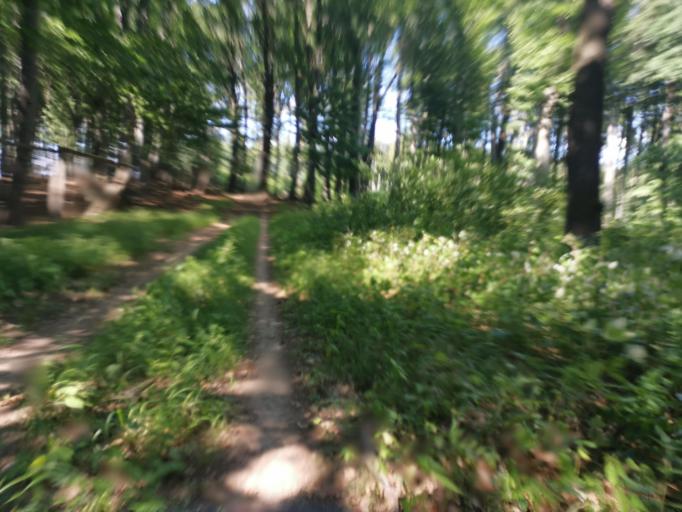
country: CZ
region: South Moravian
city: Knezdub
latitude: 48.8189
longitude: 17.4026
